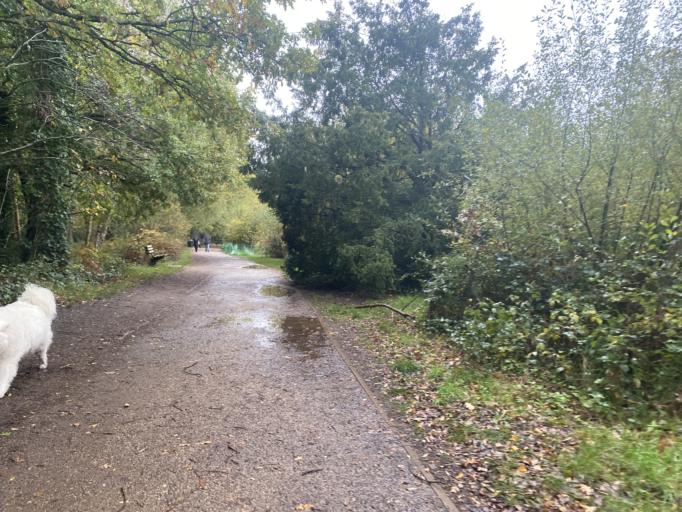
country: GB
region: England
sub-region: Hampshire
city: Petersfield
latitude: 50.9996
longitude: -0.9262
